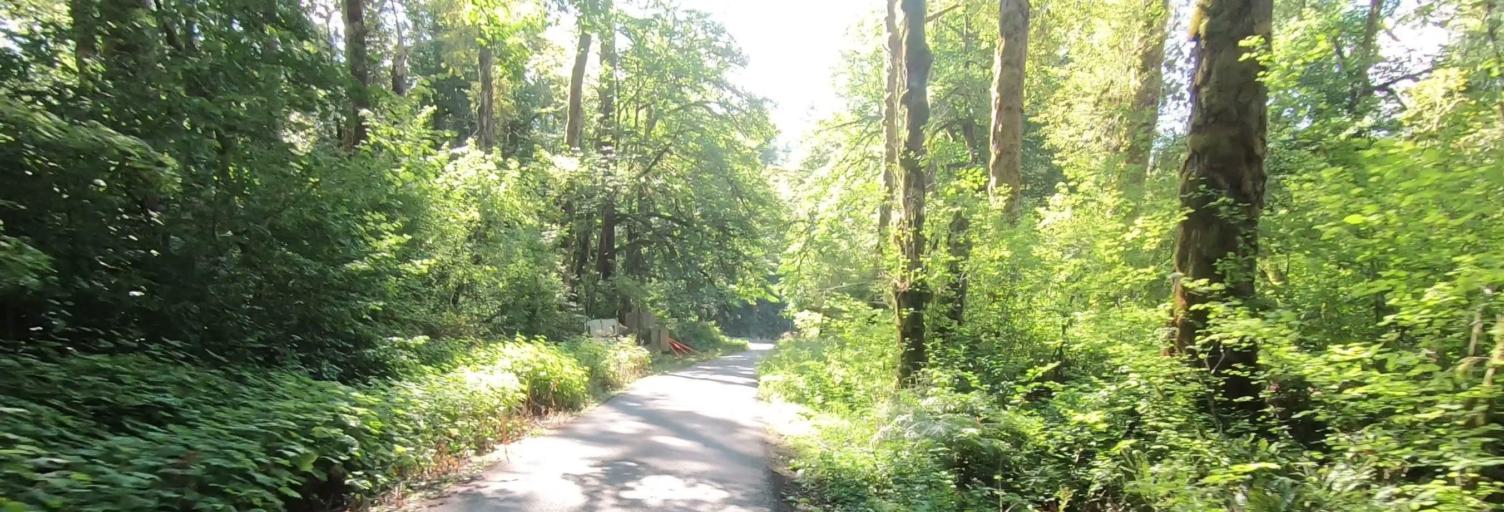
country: US
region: Washington
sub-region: Whatcom County
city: Peaceful Valley
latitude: 48.9014
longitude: -121.9341
